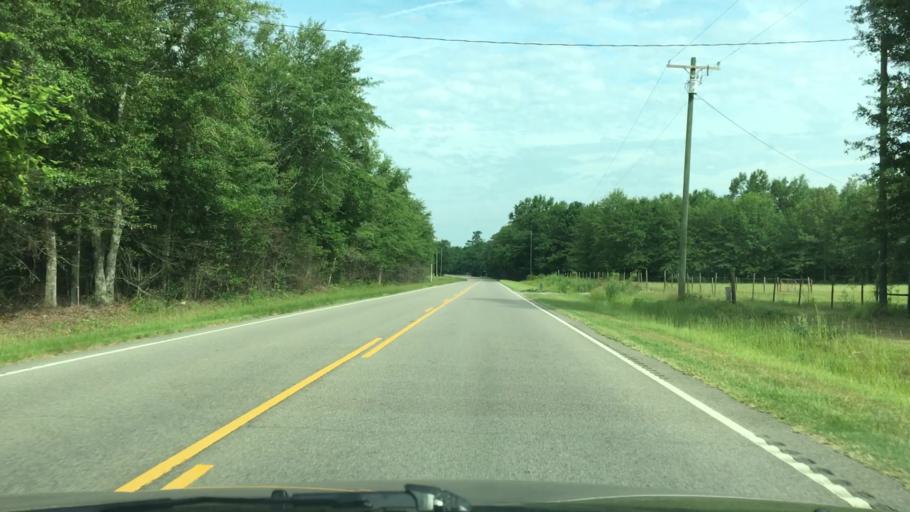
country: US
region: South Carolina
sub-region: Barnwell County
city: Williston
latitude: 33.6652
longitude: -81.3958
